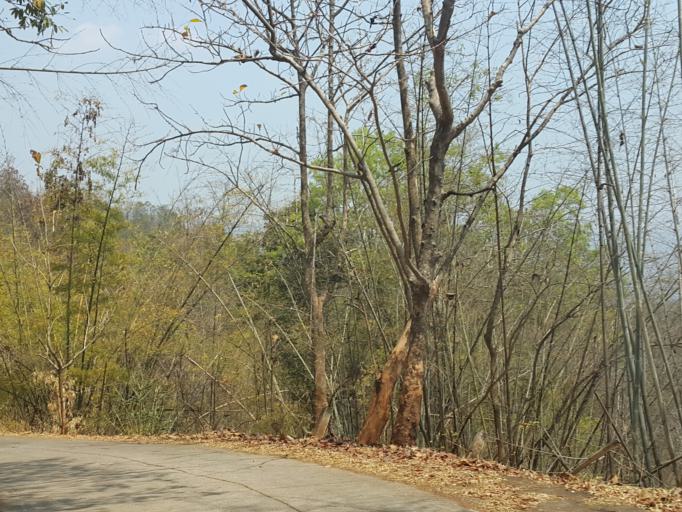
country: TH
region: Chiang Mai
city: Samoeng
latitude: 18.8040
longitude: 98.8071
